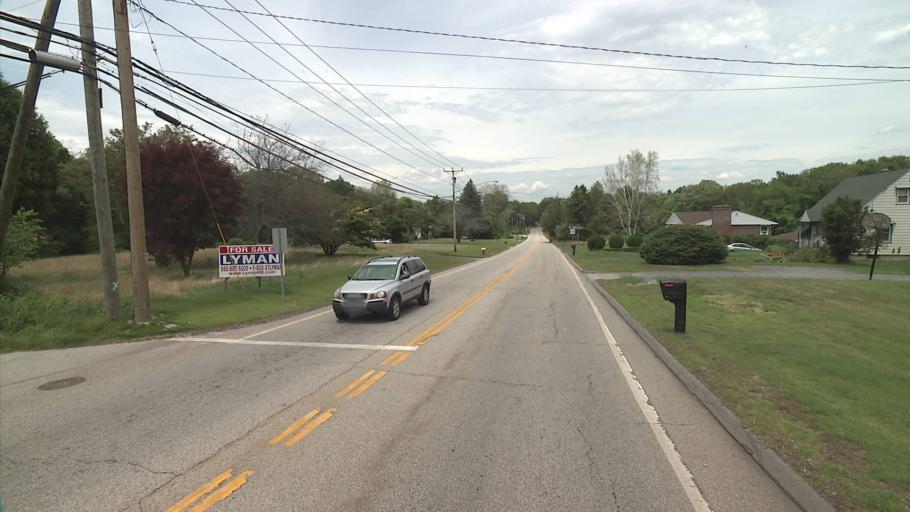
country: US
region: Connecticut
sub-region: New London County
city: Jewett City
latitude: 41.5917
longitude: -71.9761
